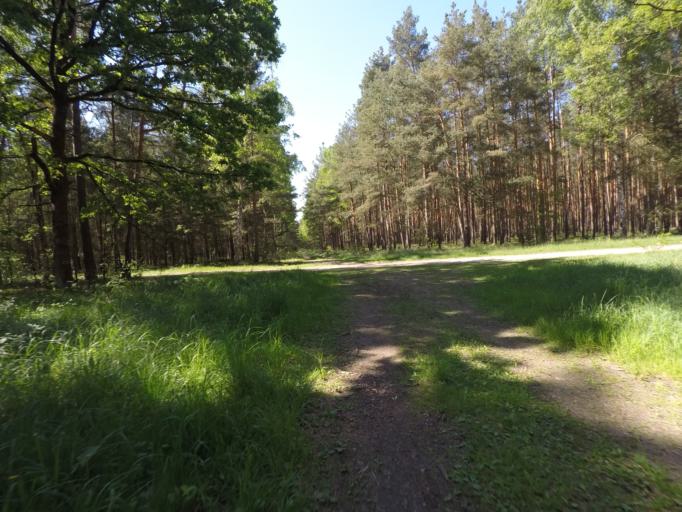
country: DE
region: Brandenburg
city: Eberswalde
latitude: 52.8173
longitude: 13.7616
